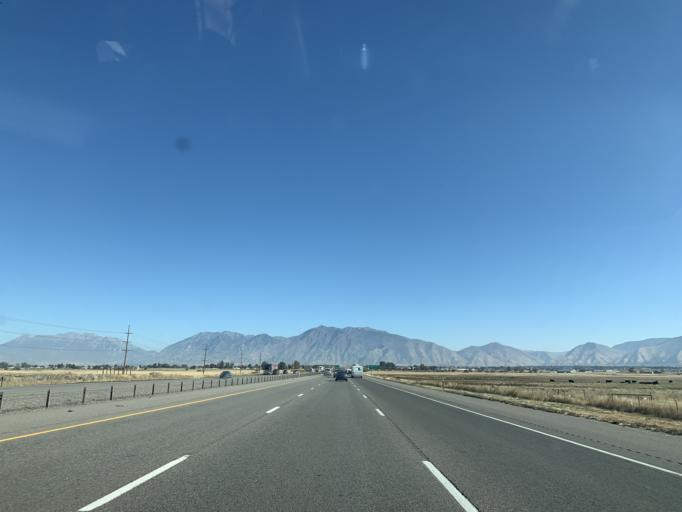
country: US
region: Utah
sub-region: Utah County
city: Payson
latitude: 40.0654
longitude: -111.7230
